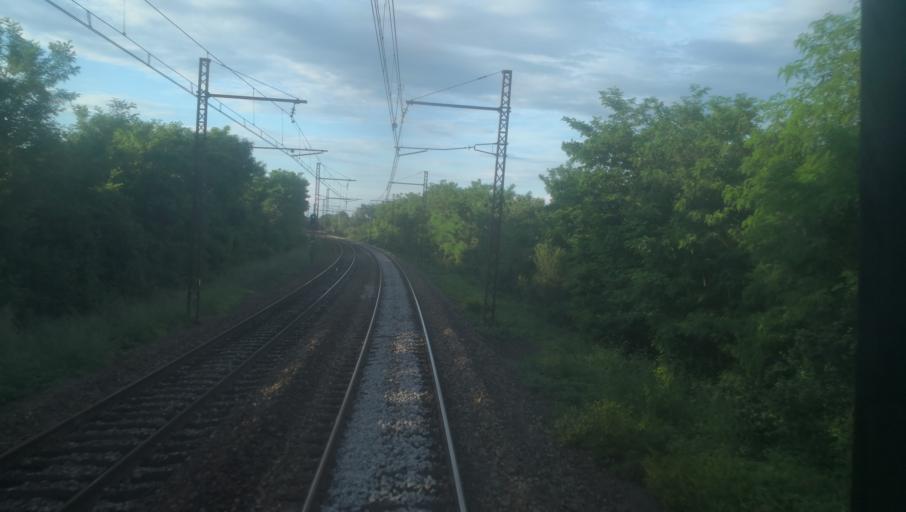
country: FR
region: Centre
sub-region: Departement de l'Indre
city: Le Pechereau
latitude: 46.5320
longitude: 1.5339
